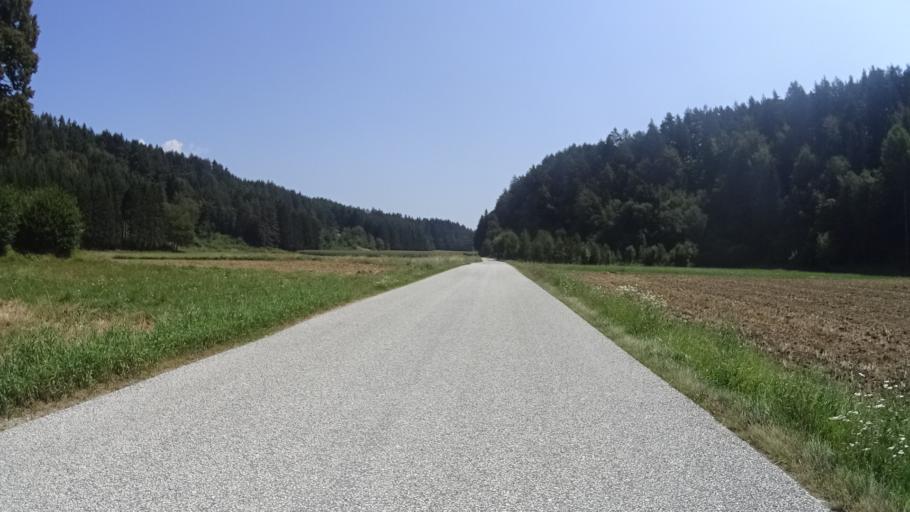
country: AT
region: Carinthia
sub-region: Politischer Bezirk Volkermarkt
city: Globasnitz
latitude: 46.5598
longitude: 14.6809
